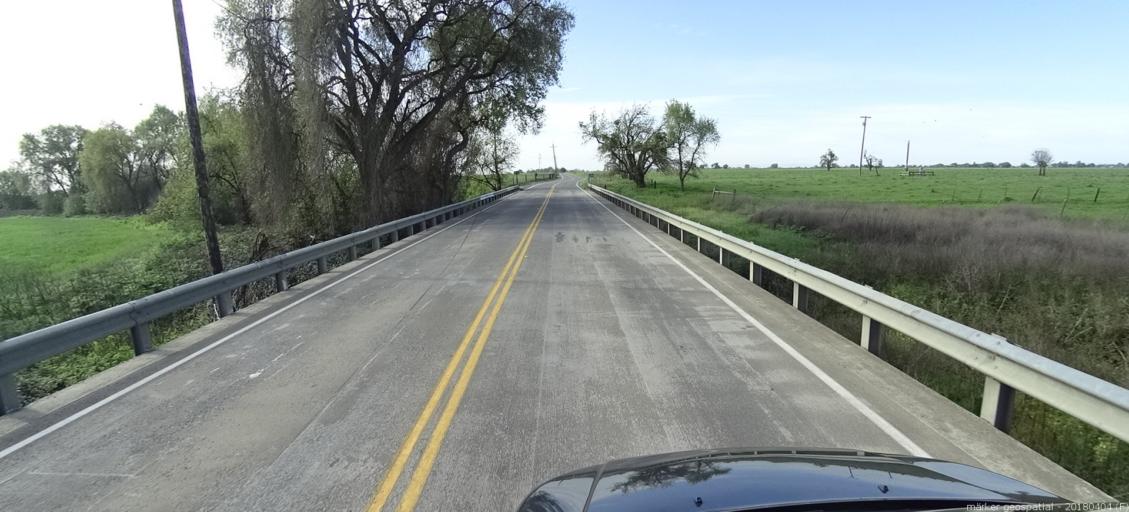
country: US
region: California
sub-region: San Joaquin County
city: Collierville
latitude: 38.2458
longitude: -121.2267
